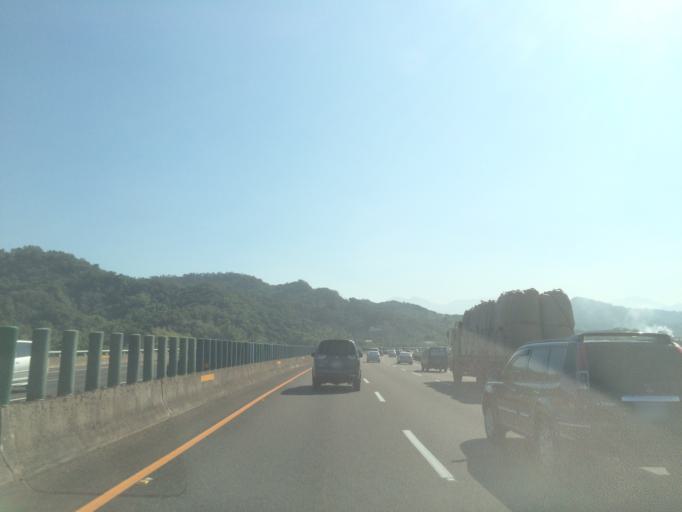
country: TW
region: Taiwan
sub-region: Nantou
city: Nantou
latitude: 23.9113
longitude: 120.6979
